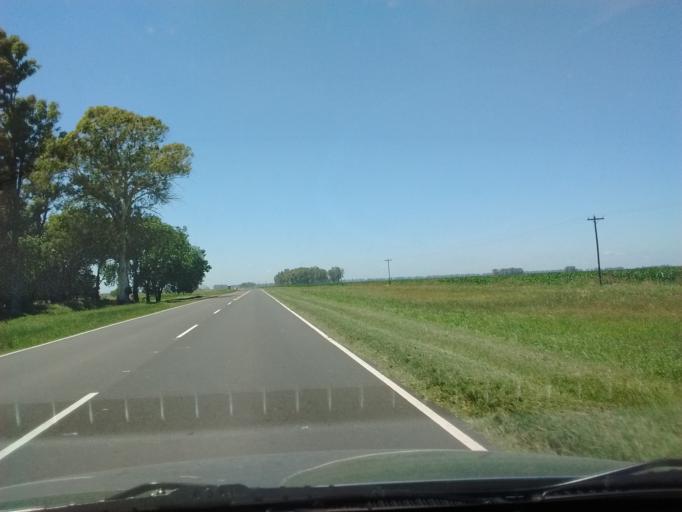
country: AR
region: Entre Rios
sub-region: Departamento de Gualeguay
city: Gualeguay
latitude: -32.9750
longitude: -59.5592
